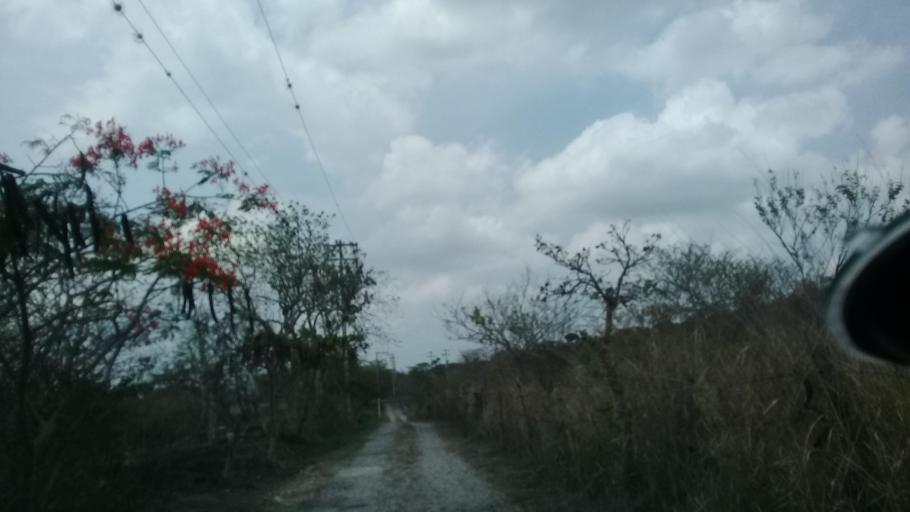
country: MX
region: Veracruz
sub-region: Emiliano Zapata
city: Plan del Rio
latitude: 19.4266
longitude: -96.6949
